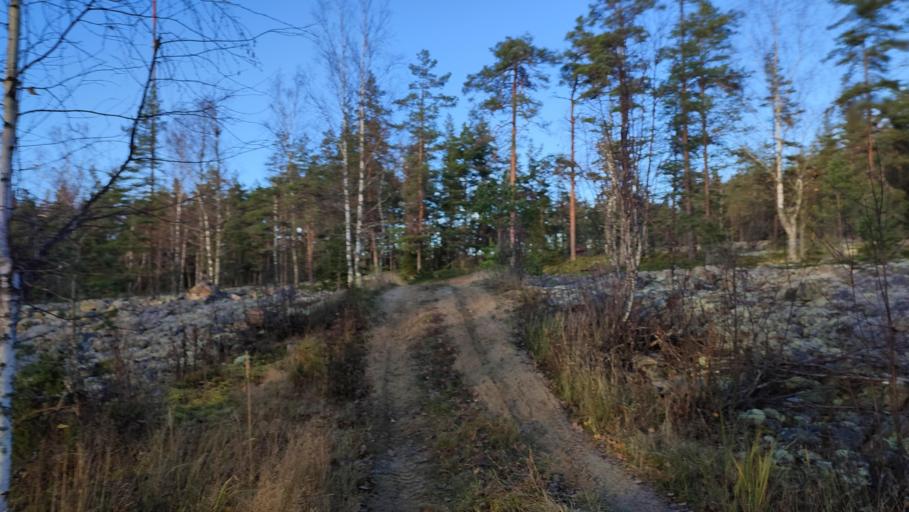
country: FI
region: Southern Ostrobothnia
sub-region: Suupohja
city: Karijoki
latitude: 62.2824
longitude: 21.6437
